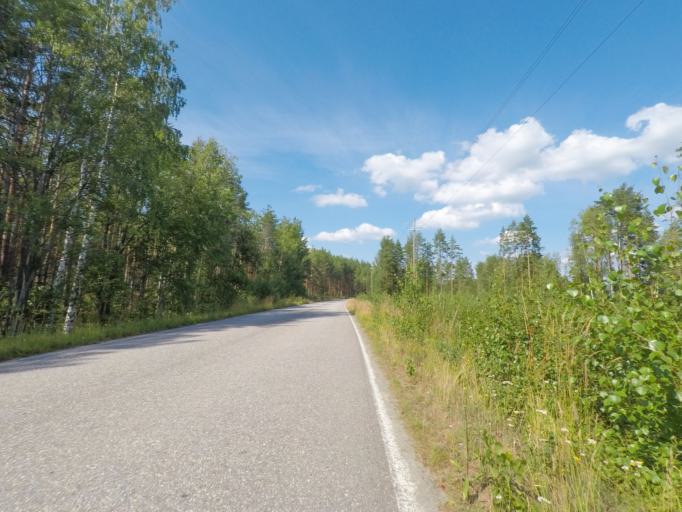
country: FI
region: Southern Savonia
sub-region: Mikkeli
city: Puumala
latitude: 61.4739
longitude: 28.1692
